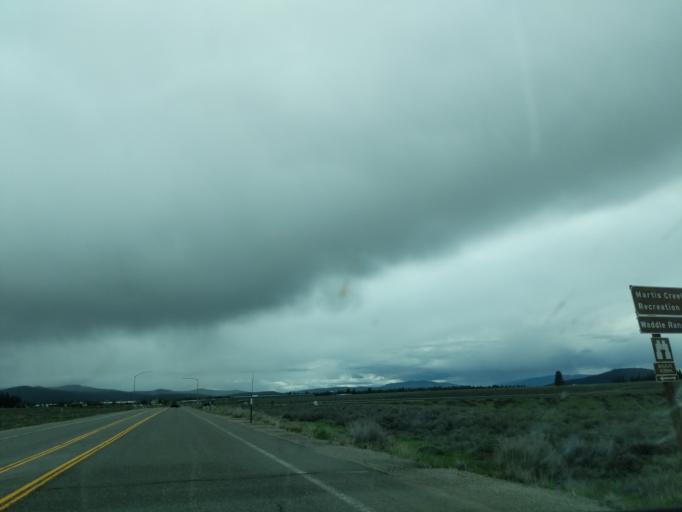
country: US
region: California
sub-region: Nevada County
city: Truckee
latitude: 39.3061
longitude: -120.1353
